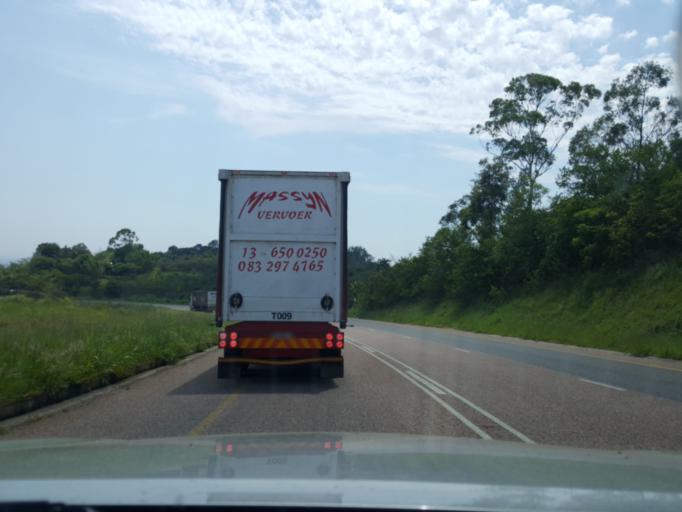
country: ZA
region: Mpumalanga
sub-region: Ehlanzeni District
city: White River
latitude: -25.1147
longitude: 31.0586
